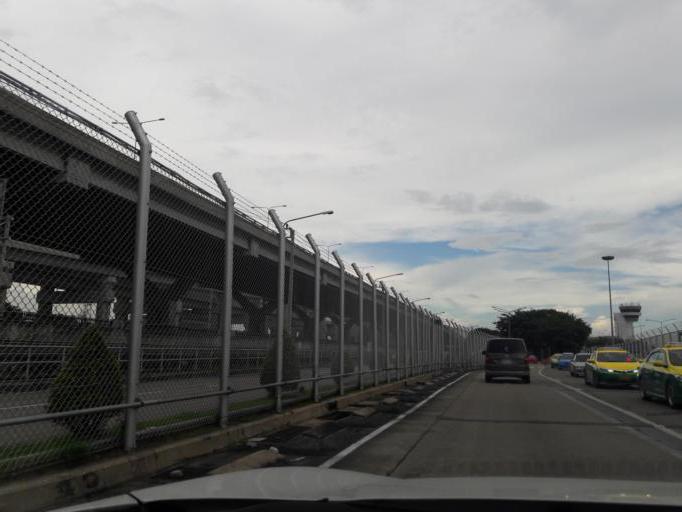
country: TH
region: Bangkok
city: Don Mueang
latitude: 13.9078
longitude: 100.5951
